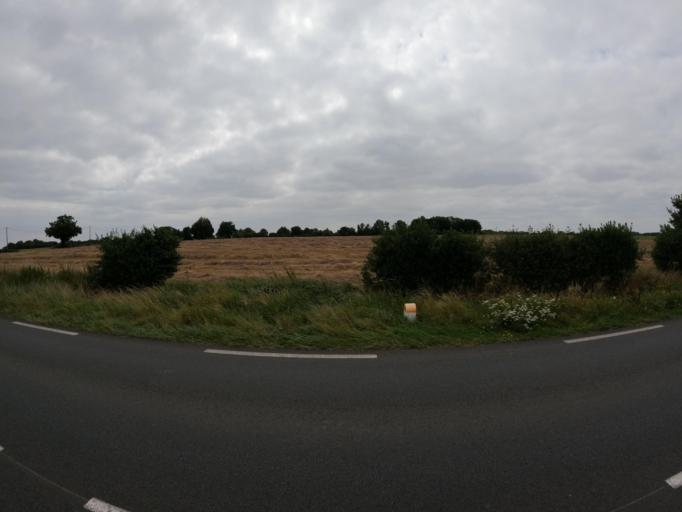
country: FR
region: Poitou-Charentes
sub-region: Departement des Deux-Sevres
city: Sauze-Vaussais
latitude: 46.1448
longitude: 0.0799
